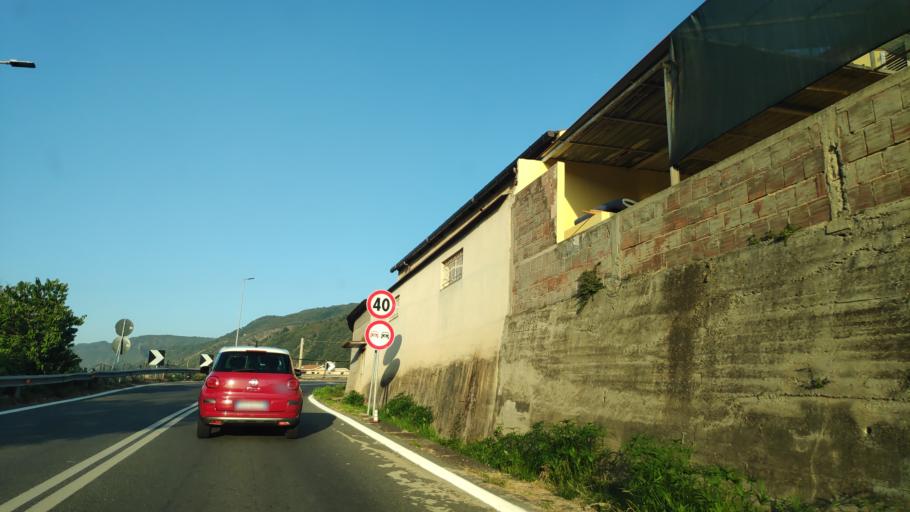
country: IT
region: Calabria
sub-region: Provincia di Reggio Calabria
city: Scilla
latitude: 38.2504
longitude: 15.7210
